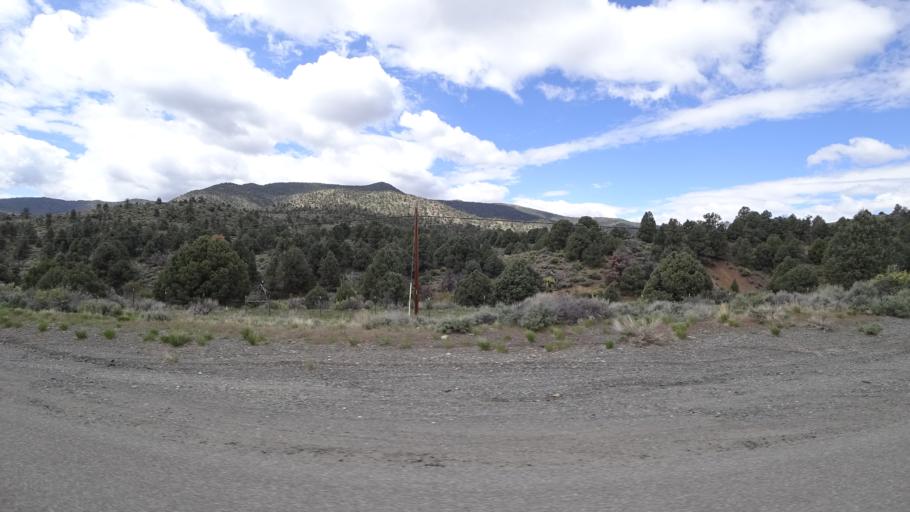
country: US
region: Nevada
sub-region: Douglas County
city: Gardnerville Ranchos
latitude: 38.7658
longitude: -119.5783
